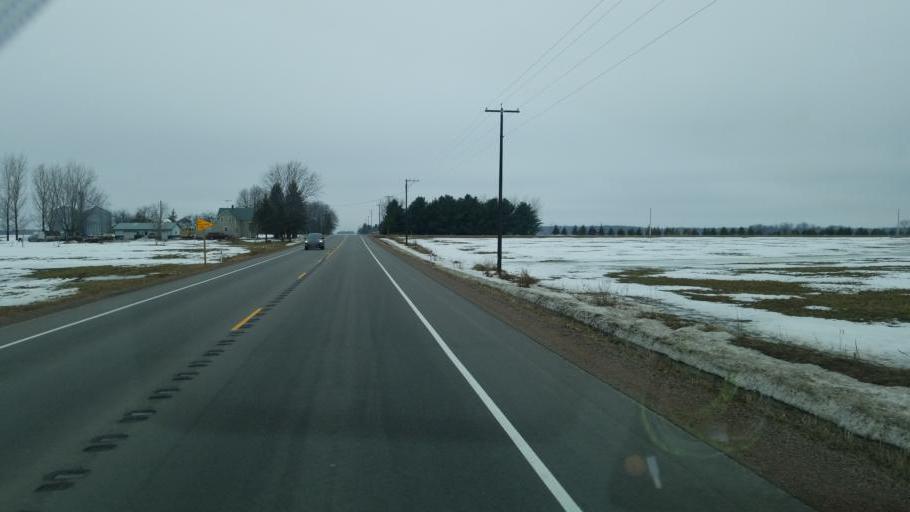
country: US
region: Wisconsin
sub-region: Marathon County
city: Spencer
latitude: 44.6563
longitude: -90.2867
